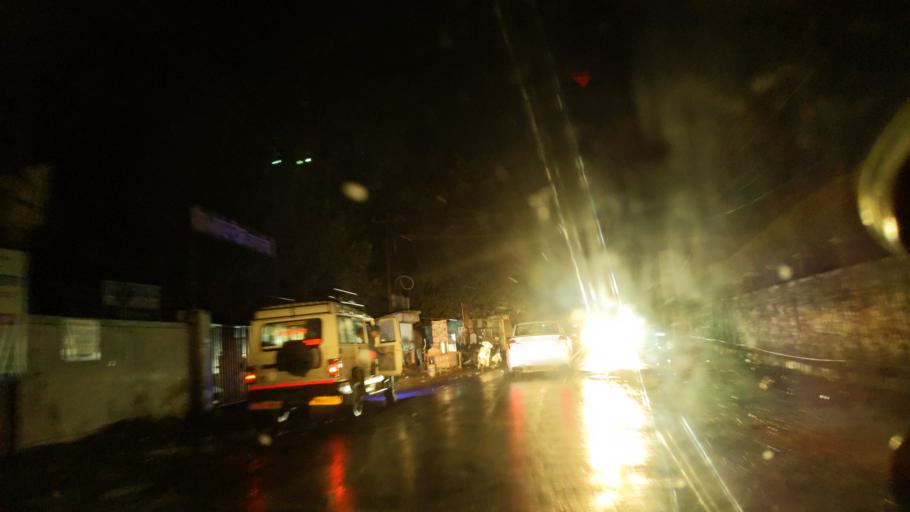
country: IN
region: Uttarakhand
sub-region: Naini Tal
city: Haldwani
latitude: 29.2066
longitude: 79.5139
